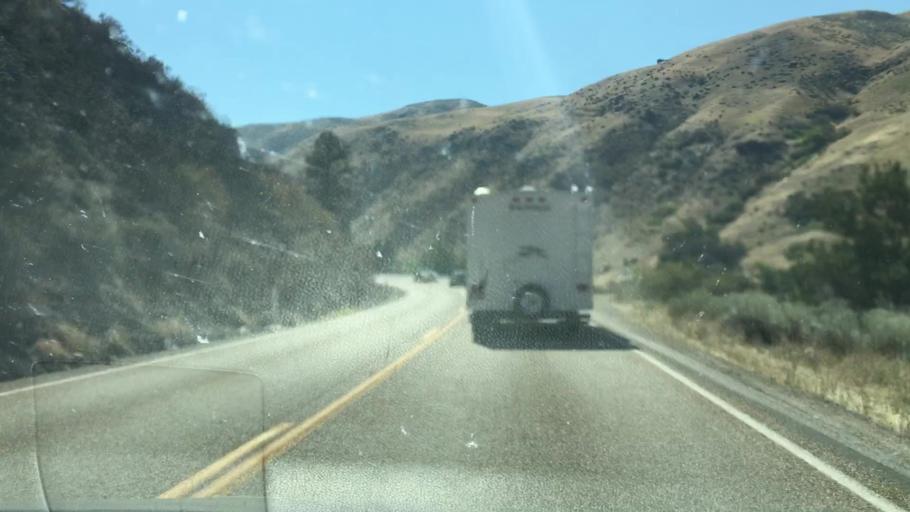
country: US
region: Idaho
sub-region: Gem County
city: Emmett
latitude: 44.0073
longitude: -116.1751
